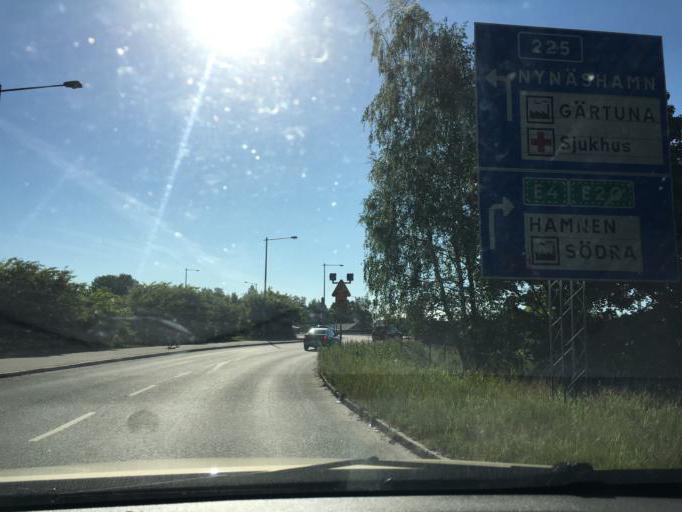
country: SE
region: Stockholm
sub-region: Sodertalje Kommun
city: Soedertaelje
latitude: 59.1891
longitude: 17.6445
